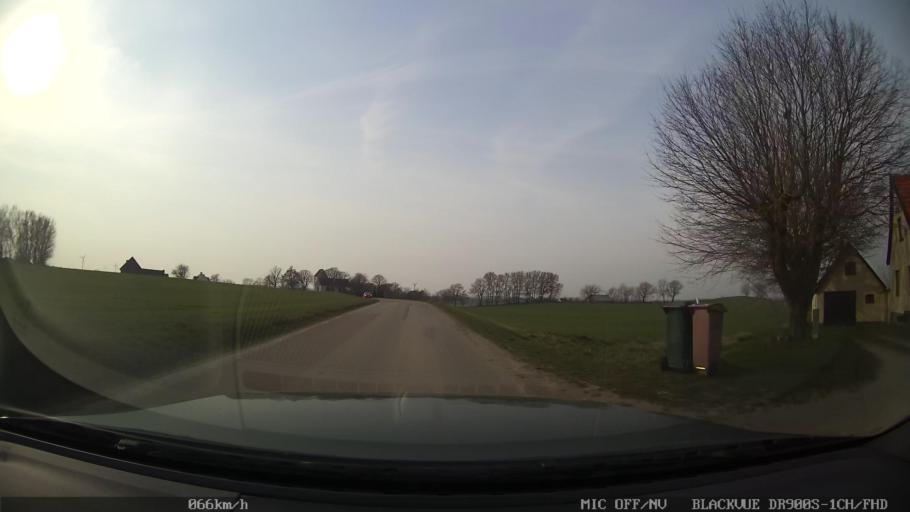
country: SE
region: Skane
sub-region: Ystads Kommun
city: Ystad
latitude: 55.4694
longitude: 13.8052
